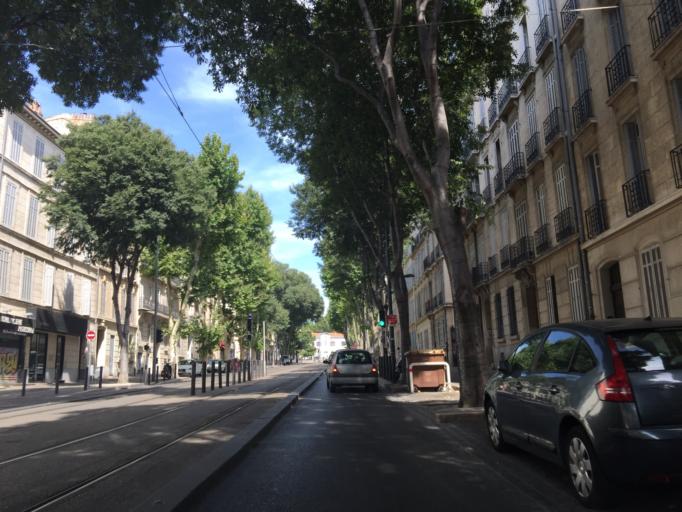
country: FR
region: Provence-Alpes-Cote d'Azur
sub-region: Departement des Bouches-du-Rhone
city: Marseille 05
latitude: 43.2960
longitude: 5.4037
